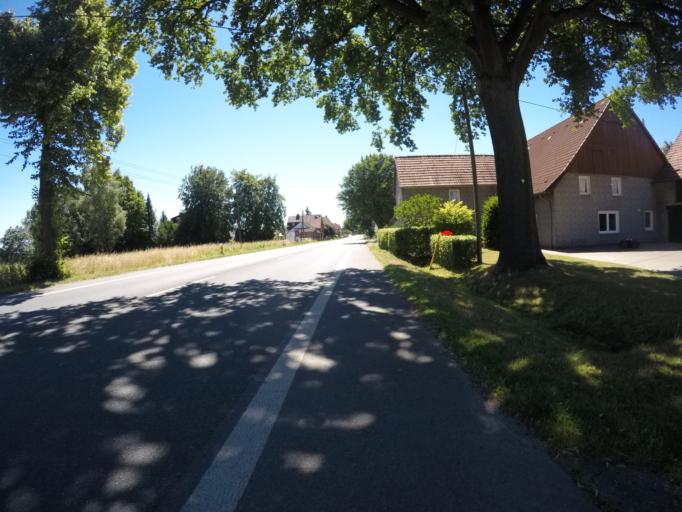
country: DE
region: North Rhine-Westphalia
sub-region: Regierungsbezirk Detmold
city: Bielefeld
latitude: 52.0735
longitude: 8.5804
